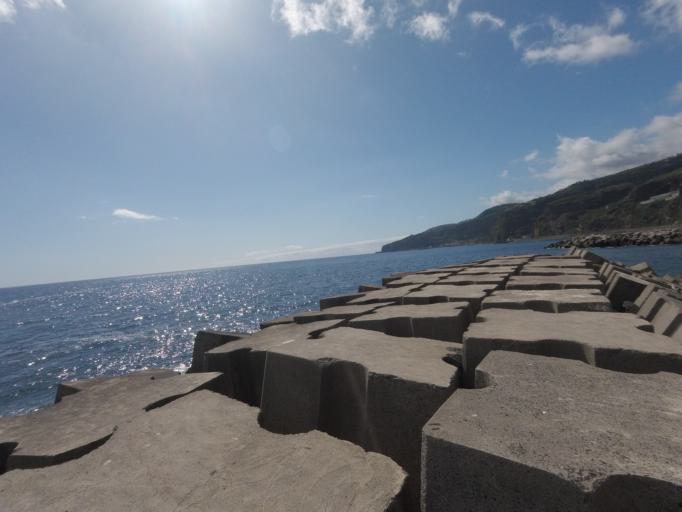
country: PT
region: Madeira
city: Ribeira Brava
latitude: 32.6689
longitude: -17.0659
